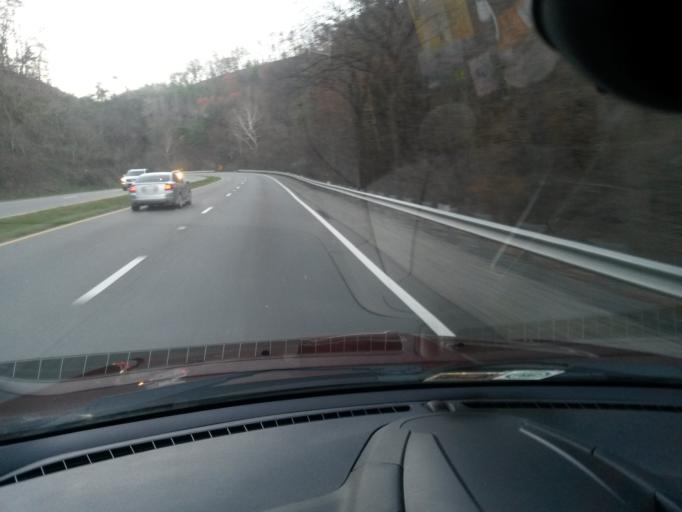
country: US
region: Virginia
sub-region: Roanoke County
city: Narrows
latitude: 37.1966
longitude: -79.9428
